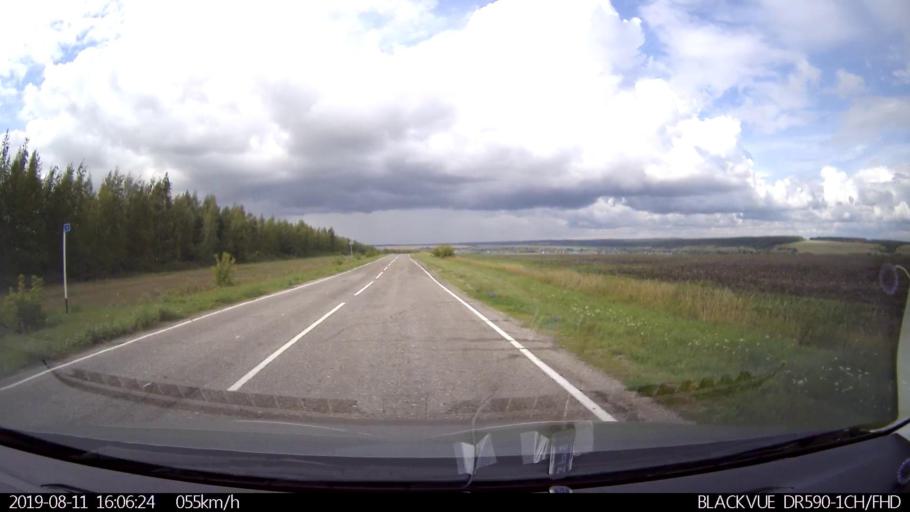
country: RU
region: Ulyanovsk
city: Ignatovka
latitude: 53.9686
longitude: 47.6487
